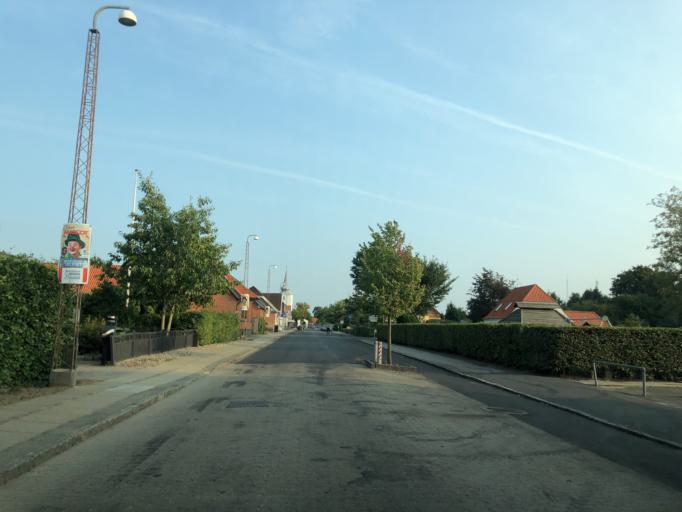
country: DK
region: South Denmark
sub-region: Vejle Kommune
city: Jelling
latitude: 55.7043
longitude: 9.3785
